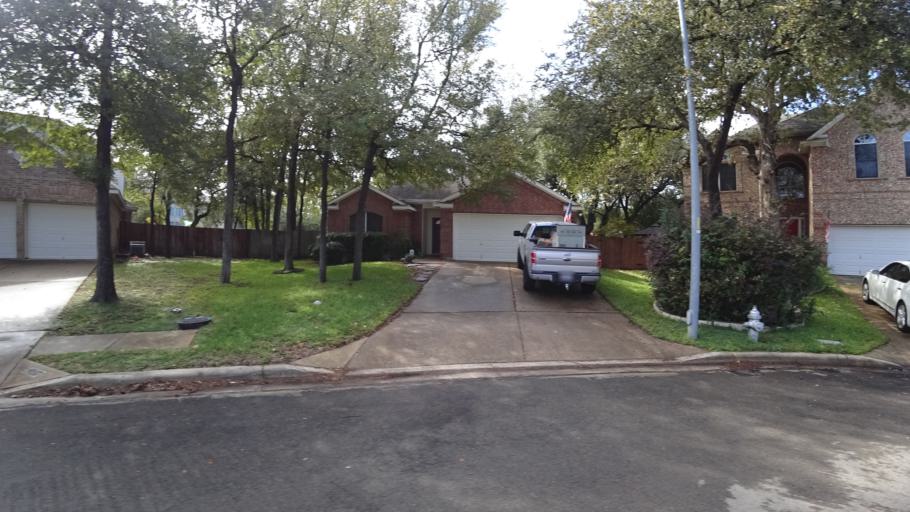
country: US
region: Texas
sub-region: Travis County
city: Shady Hollow
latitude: 30.2036
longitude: -97.8716
